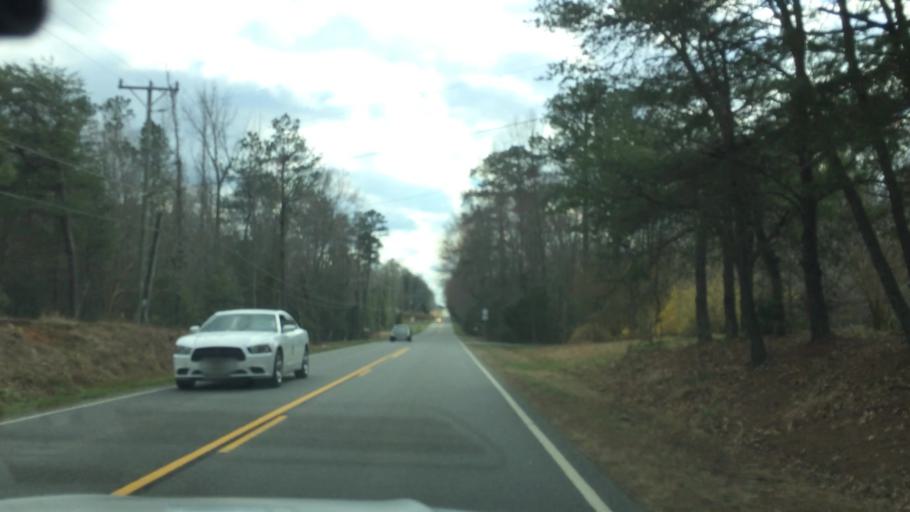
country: US
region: Virginia
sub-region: New Kent County
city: New Kent
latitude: 37.5133
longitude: -77.0142
